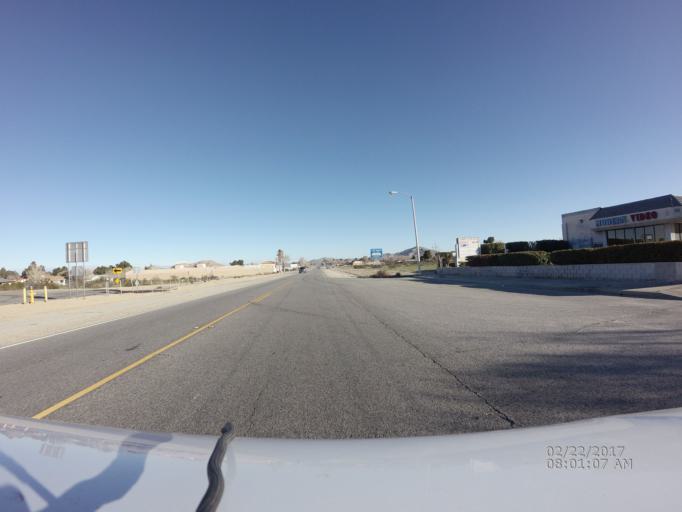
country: US
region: California
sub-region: Los Angeles County
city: Lake Los Angeles
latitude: 34.6108
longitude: -117.8262
